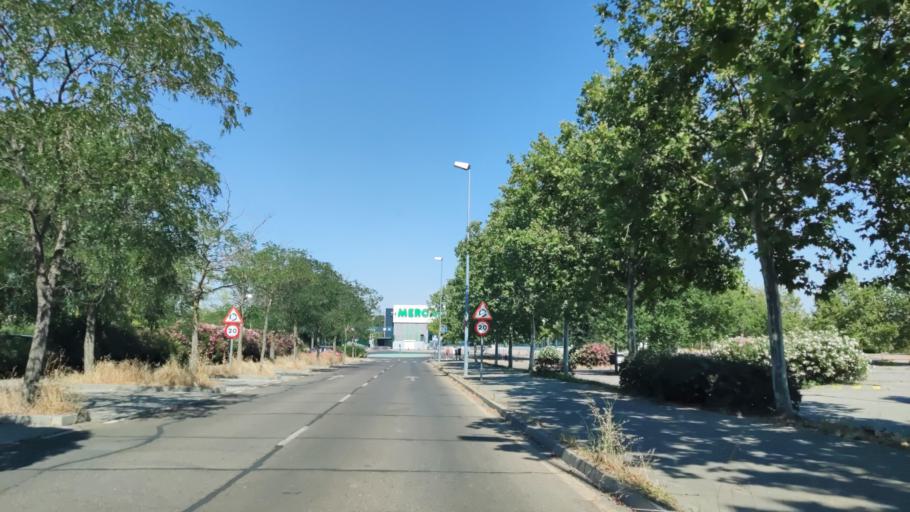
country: ES
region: Madrid
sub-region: Provincia de Madrid
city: Leganes
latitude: 40.3415
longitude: -3.7593
